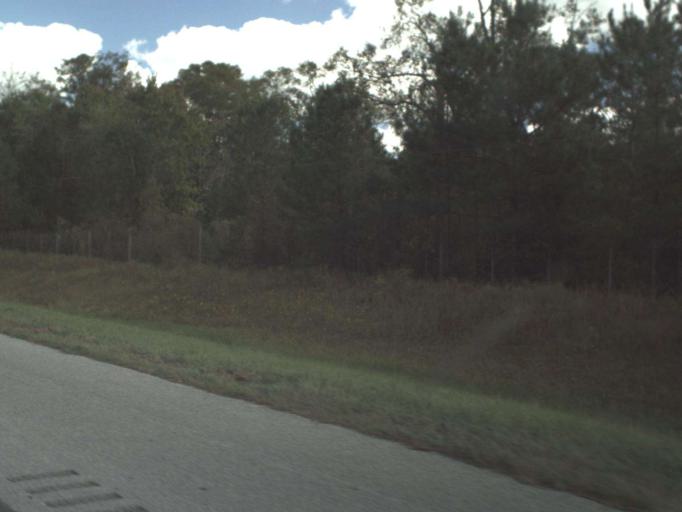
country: US
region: Florida
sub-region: Jackson County
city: Sneads
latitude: 30.6360
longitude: -84.9330
